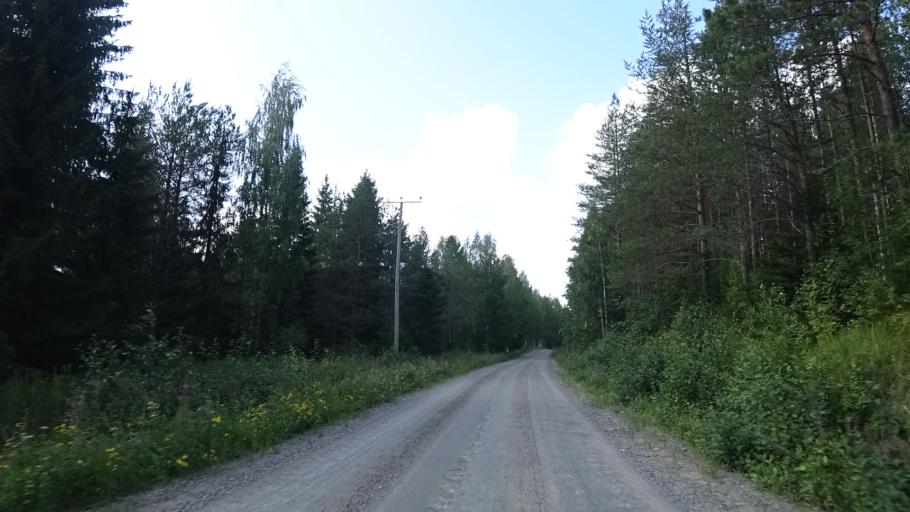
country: FI
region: North Karelia
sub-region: Joensuu
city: Ilomantsi
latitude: 62.9298
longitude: 31.3165
